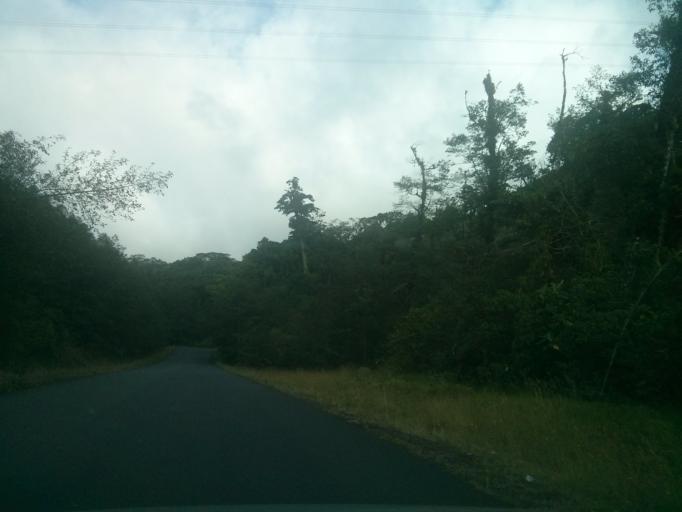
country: CR
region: Heredia
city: Santo Domingo
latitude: 10.1522
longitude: -84.1490
